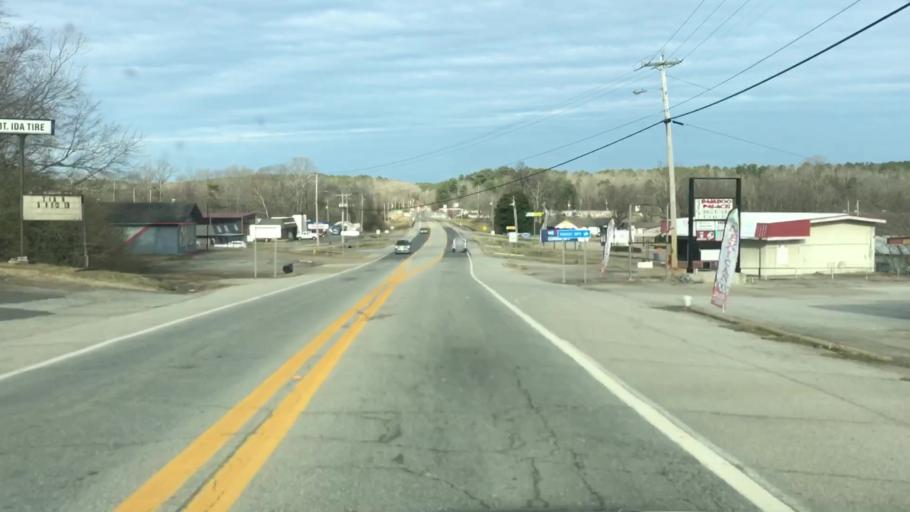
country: US
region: Arkansas
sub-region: Montgomery County
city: Mount Ida
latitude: 34.5586
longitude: -93.6331
